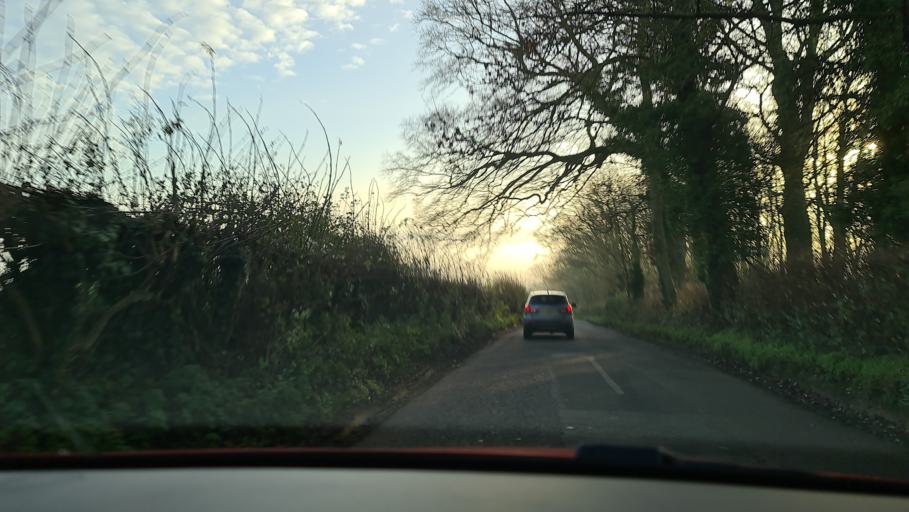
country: GB
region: England
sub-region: Buckinghamshire
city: Long Crendon
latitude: 51.8131
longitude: -0.9768
